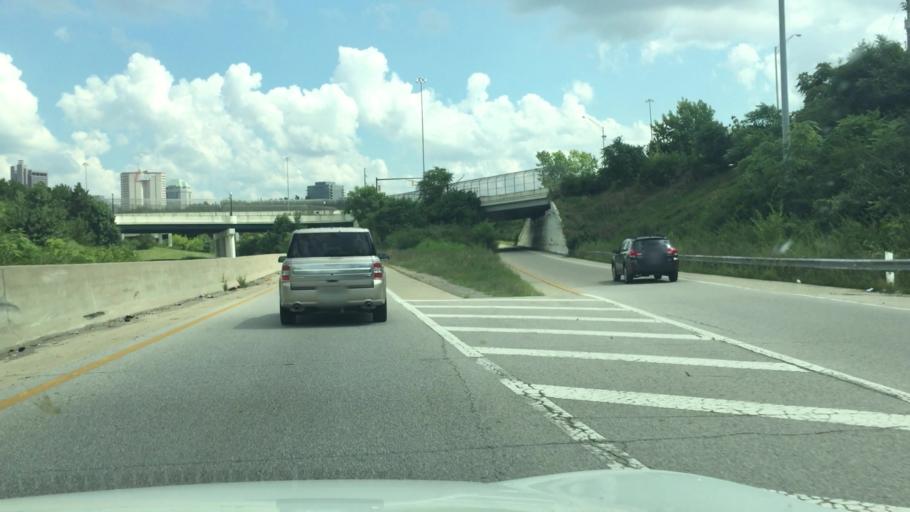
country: US
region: Ohio
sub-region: Franklin County
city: Columbus
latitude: 39.9750
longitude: -83.0173
